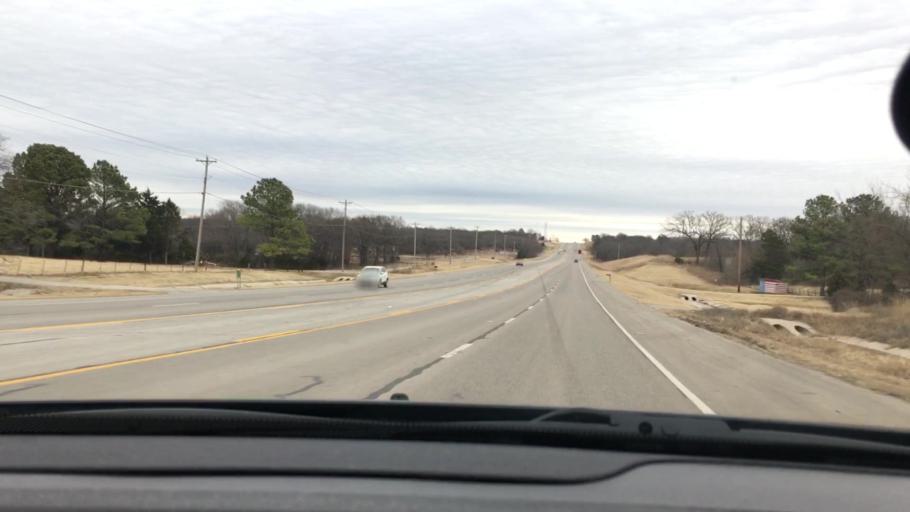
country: US
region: Oklahoma
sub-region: Carter County
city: Dickson
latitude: 34.1871
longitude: -97.0148
